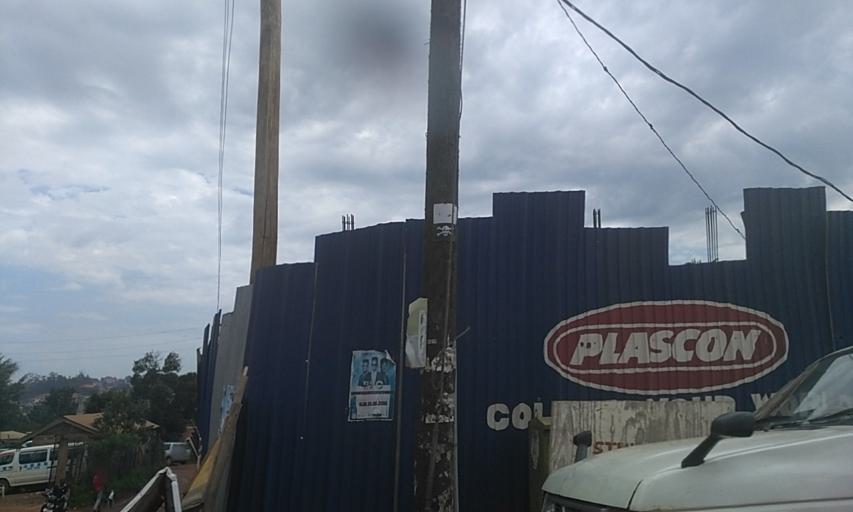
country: UG
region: Central Region
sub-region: Wakiso District
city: Bweyogerere
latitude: 0.3787
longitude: 32.6476
